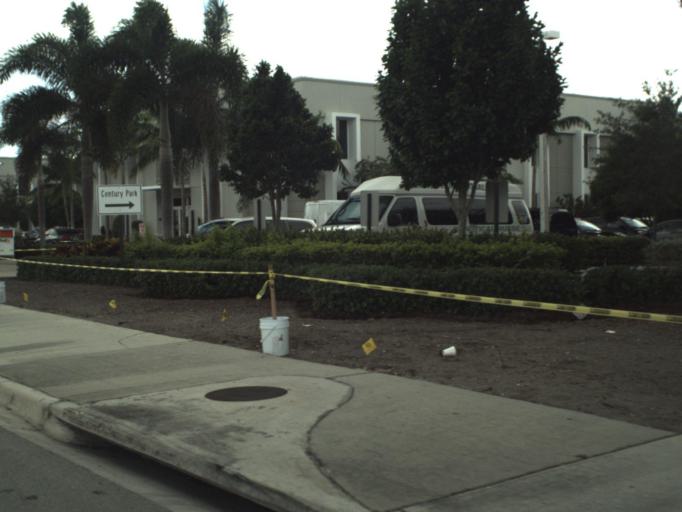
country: US
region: Florida
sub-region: Palm Beach County
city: Plantation Mobile Home Park
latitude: 26.7069
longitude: -80.1220
